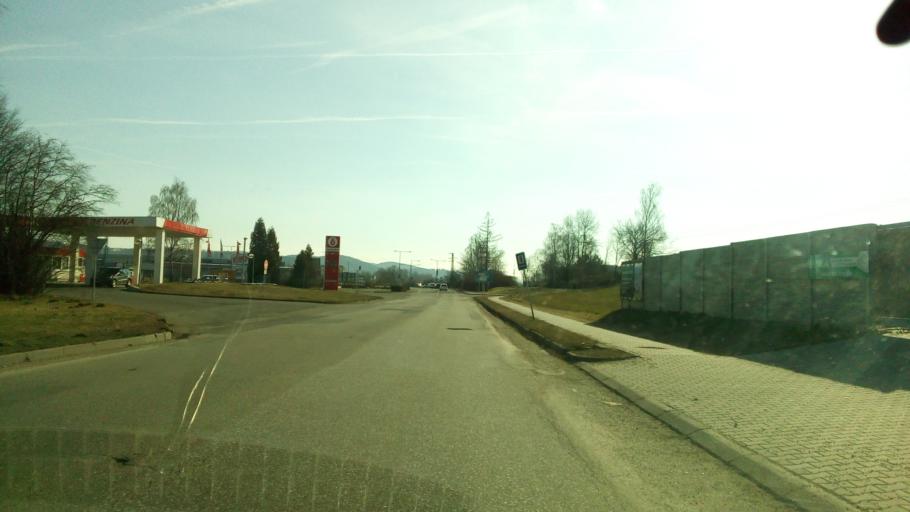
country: CZ
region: Olomoucky
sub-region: Okres Sumperk
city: Sumperk
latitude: 49.9546
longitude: 16.9608
